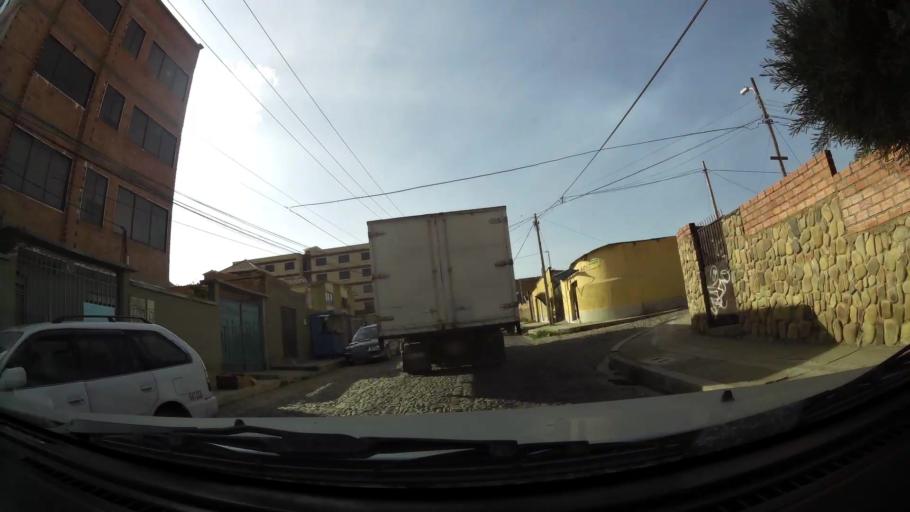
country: BO
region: La Paz
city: La Paz
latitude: -16.5189
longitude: -68.0836
